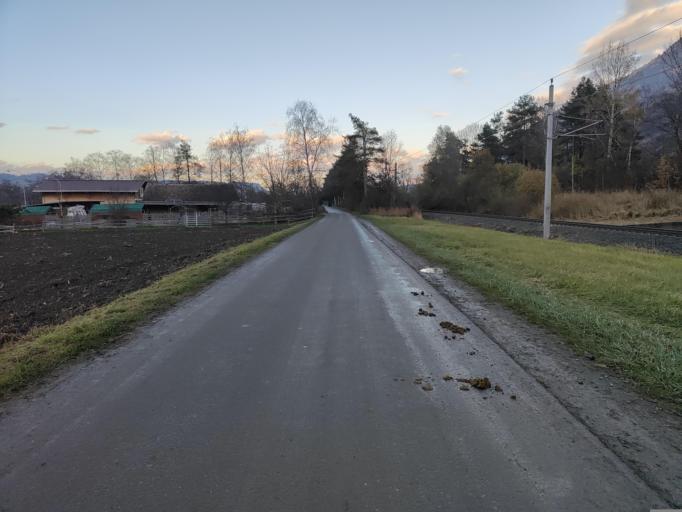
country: LI
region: Schaan
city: Schaan
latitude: 47.1819
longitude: 9.5213
